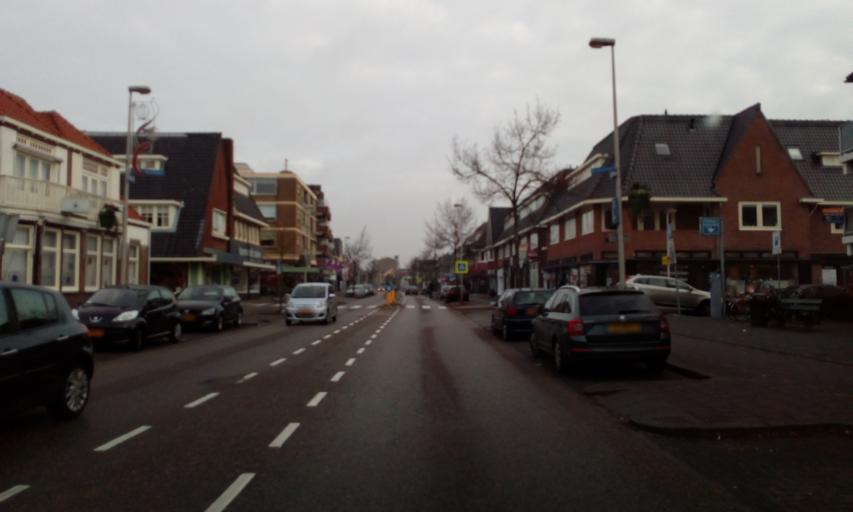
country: NL
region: North Holland
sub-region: Gemeente Bussum
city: Bussum
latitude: 52.2741
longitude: 5.1688
